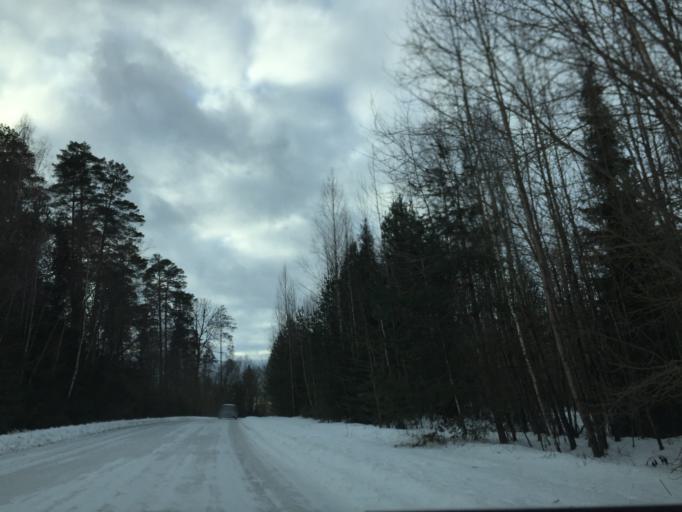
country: LV
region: Lielvarde
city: Lielvarde
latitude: 56.6196
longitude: 24.7745
